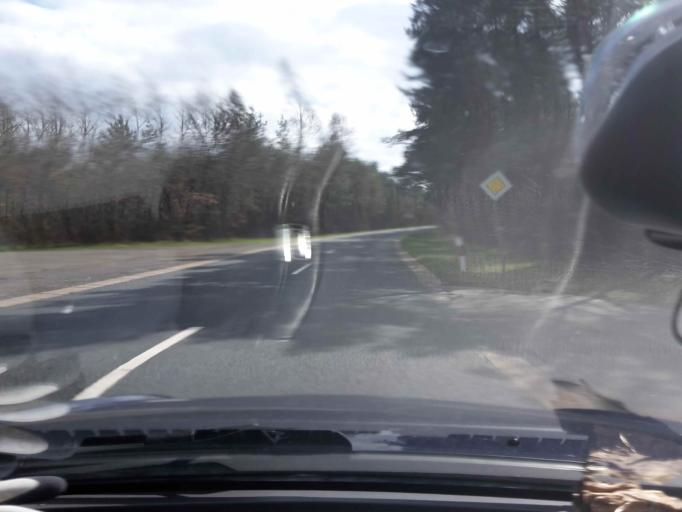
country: DE
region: Lower Saxony
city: Bispingen
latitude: 53.0876
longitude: 10.0528
